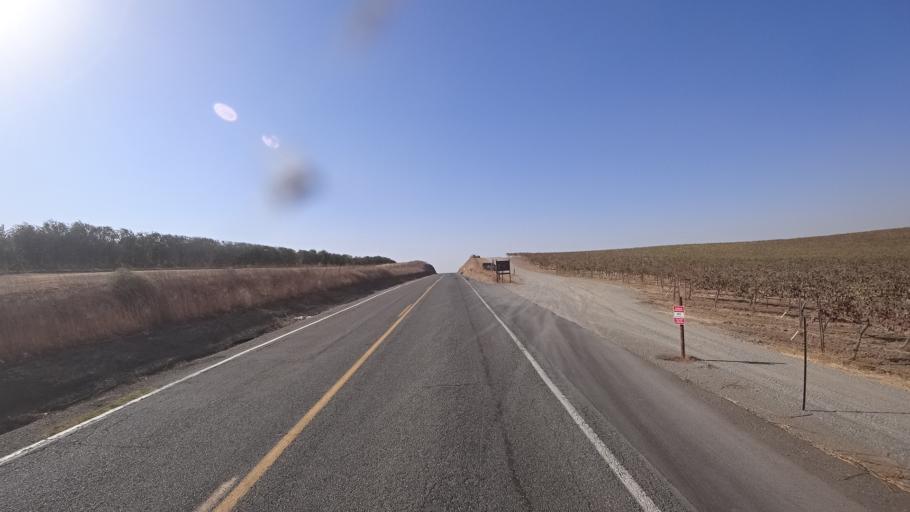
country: US
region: California
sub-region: Yolo County
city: Woodland
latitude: 38.7070
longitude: -121.8712
